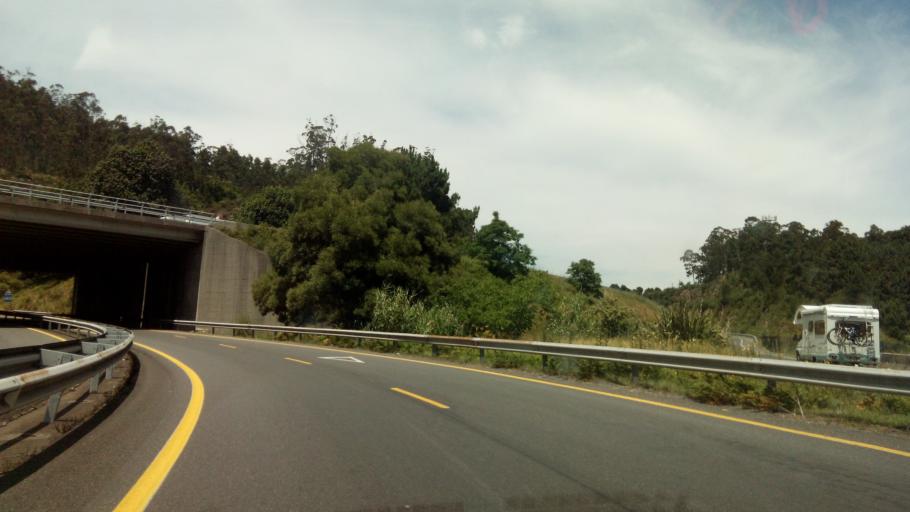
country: ES
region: Galicia
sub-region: Provincia de Pontevedra
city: Redondela
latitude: 42.2947
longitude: -8.6573
